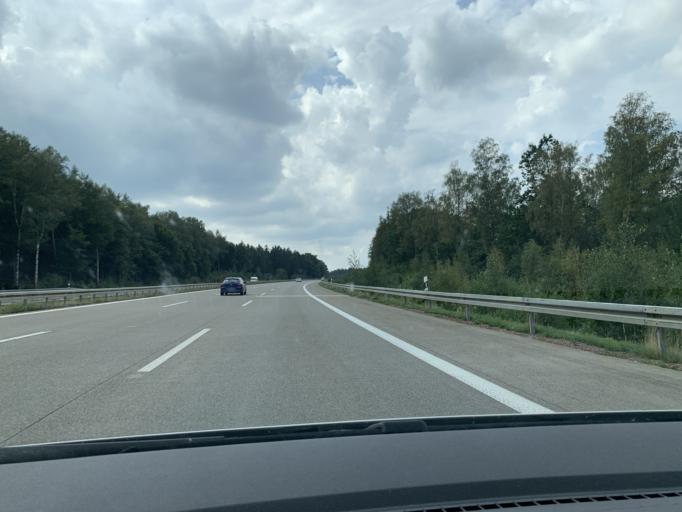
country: DE
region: Saxony
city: Limbach-Oberfrohna
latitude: 50.8302
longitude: 12.7865
